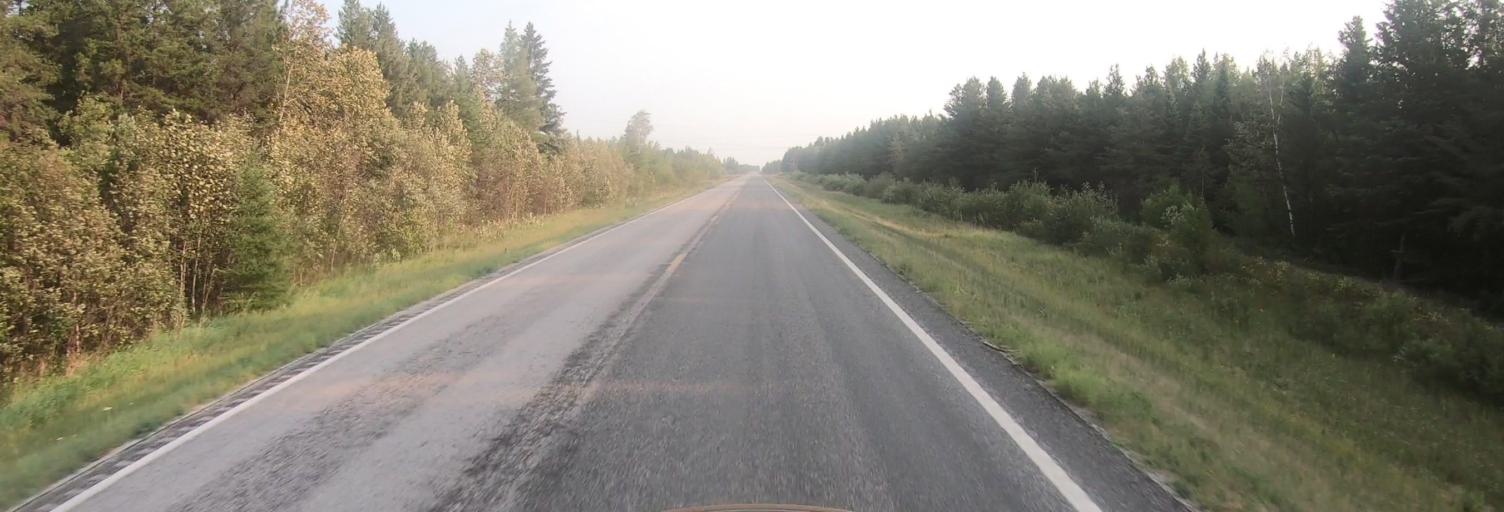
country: US
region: Minnesota
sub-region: Roseau County
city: Warroad
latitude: 48.7500
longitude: -95.3304
